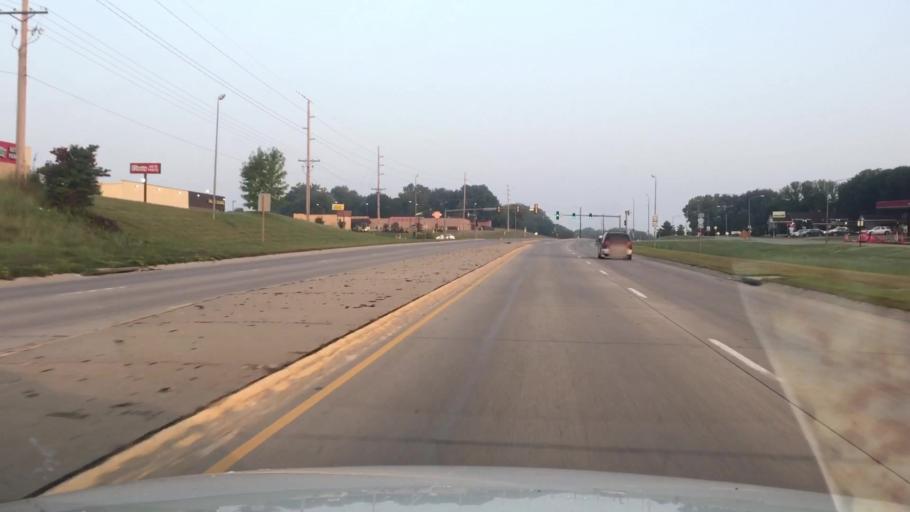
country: US
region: Iowa
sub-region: Warren County
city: Carlisle
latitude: 41.4979
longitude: -93.4958
